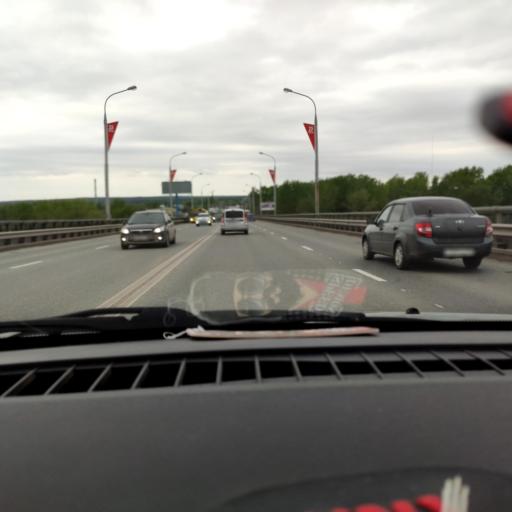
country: RU
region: Perm
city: Perm
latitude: 58.0221
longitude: 56.2215
